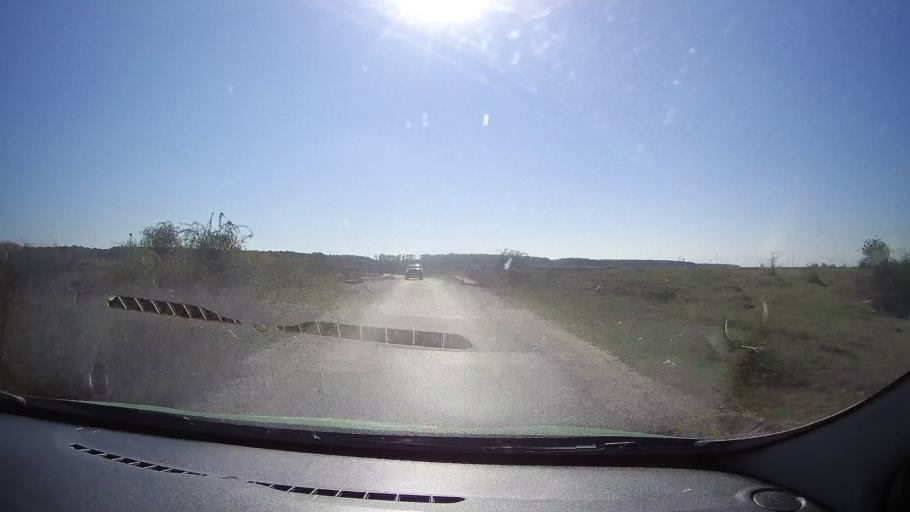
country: RO
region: Satu Mare
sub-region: Comuna Doba
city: Doba
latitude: 47.7240
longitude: 22.7243
